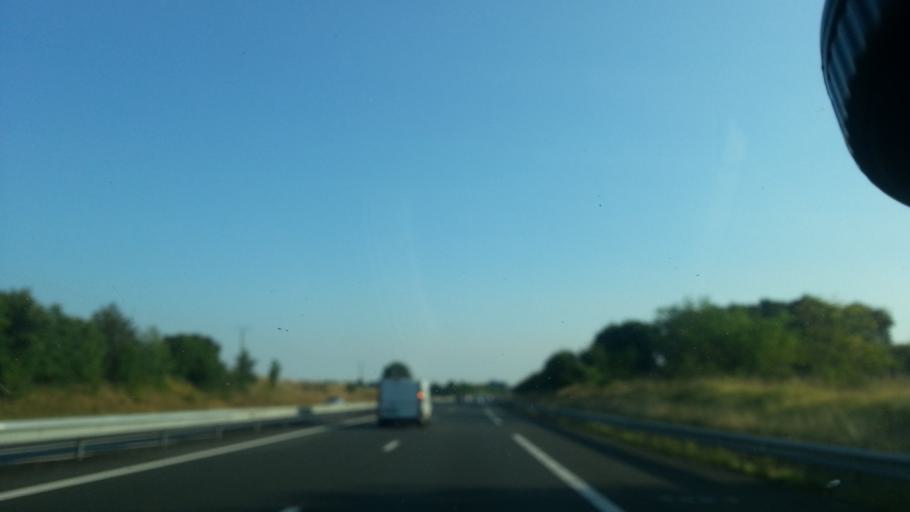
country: FR
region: Poitou-Charentes
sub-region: Departement des Deux-Sevres
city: Beauvoir-sur-Niort
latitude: 46.1069
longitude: -0.5352
